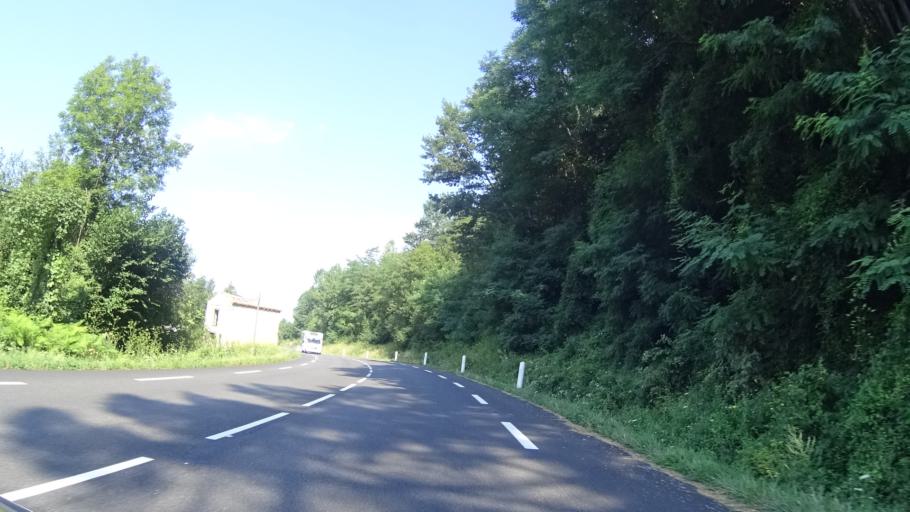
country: FR
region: Midi-Pyrenees
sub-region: Departement de l'Ariege
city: Lavelanet
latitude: 42.9135
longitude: 1.7750
